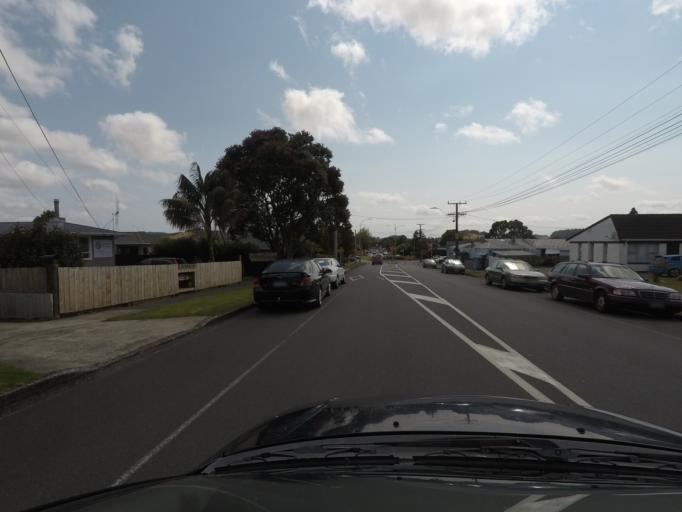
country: NZ
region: Northland
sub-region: Whangarei
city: Whangarei
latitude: -35.6867
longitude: 174.3258
